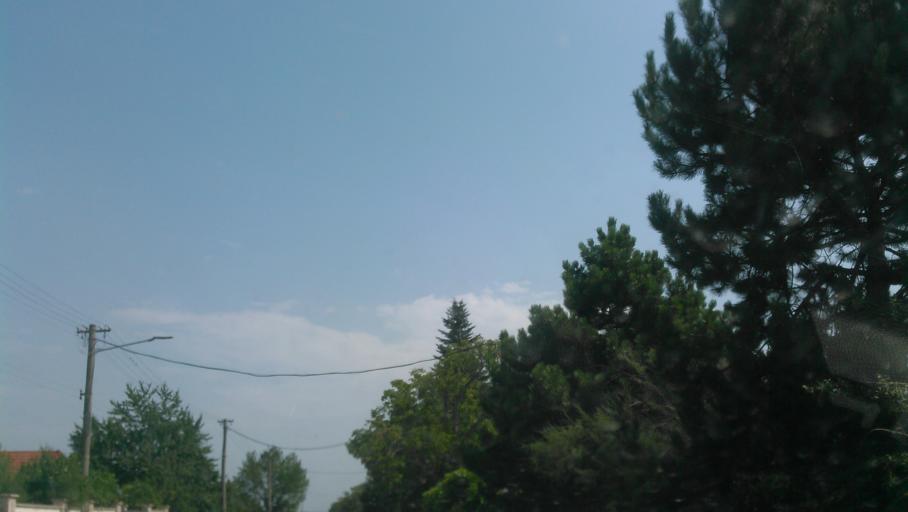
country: SK
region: Trnavsky
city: Dunajska Streda
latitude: 48.0349
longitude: 17.5331
